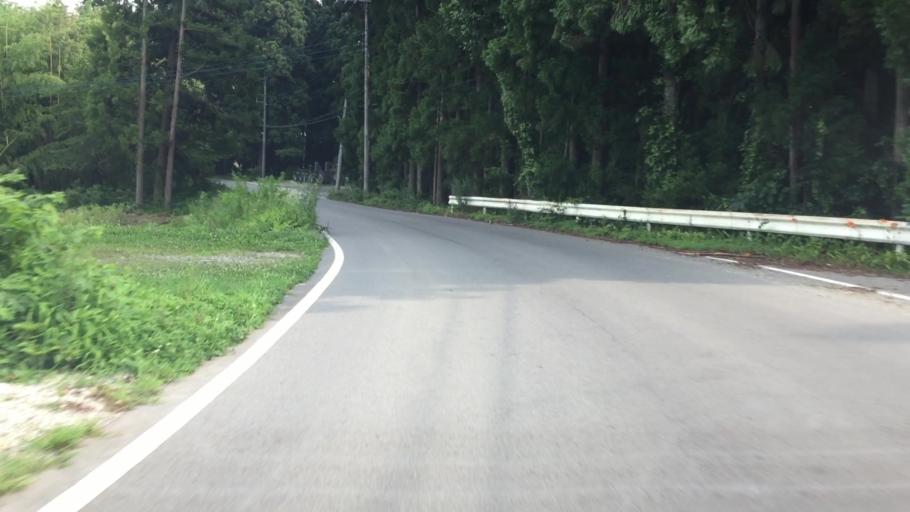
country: JP
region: Tochigi
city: Kuroiso
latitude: 36.9627
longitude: 139.9806
